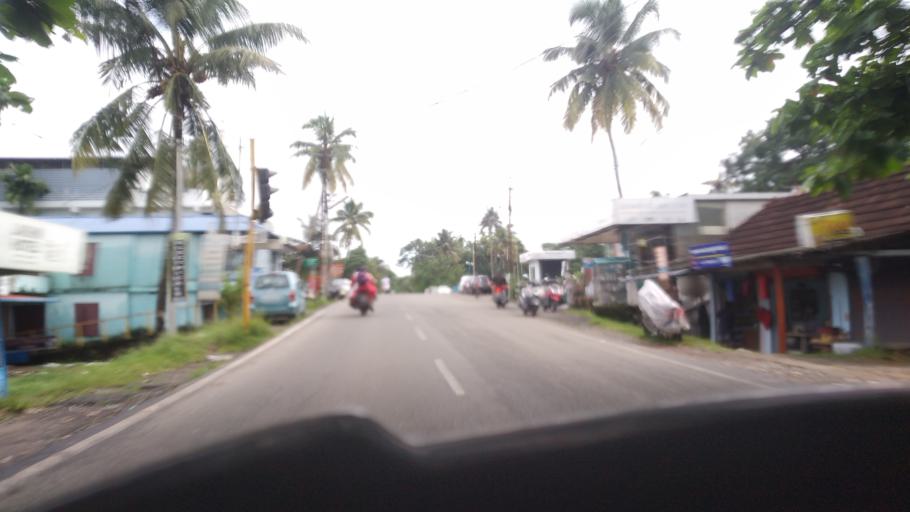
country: IN
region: Kerala
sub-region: Ernakulam
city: Elur
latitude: 10.0899
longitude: 76.2080
